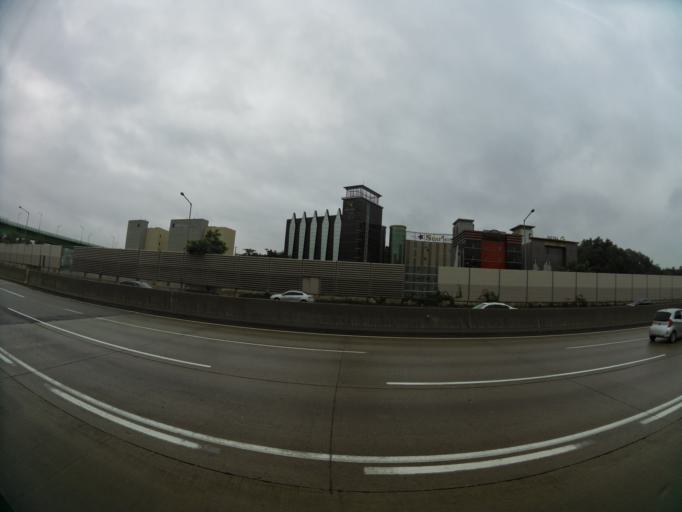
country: KR
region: Gyeonggi-do
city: Suwon-si
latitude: 37.2898
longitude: 127.0970
